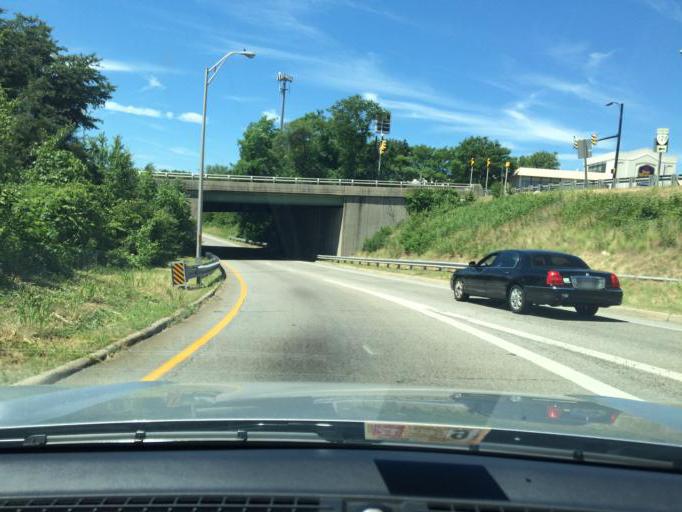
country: US
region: Virginia
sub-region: Arlington County
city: Arlington
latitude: 38.8477
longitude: -77.0791
